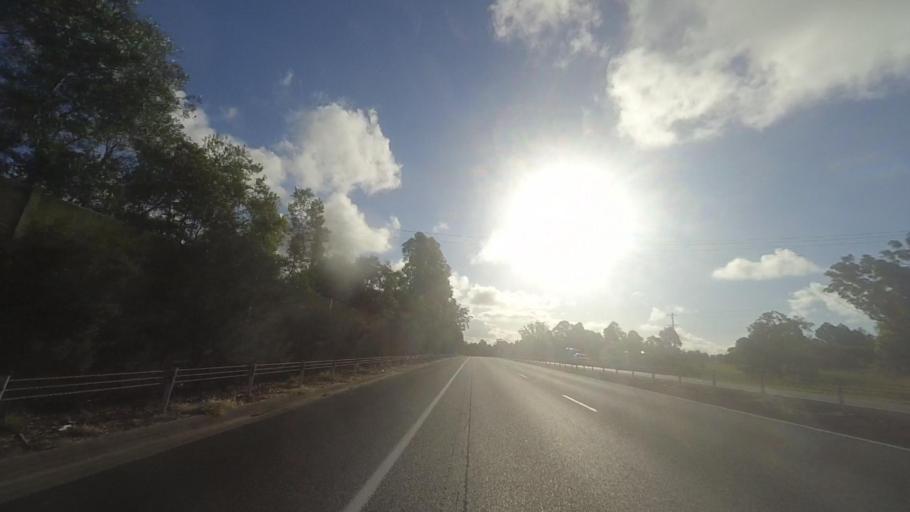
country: AU
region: New South Wales
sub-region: Great Lakes
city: Nabiac
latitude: -32.0945
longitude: 152.3824
